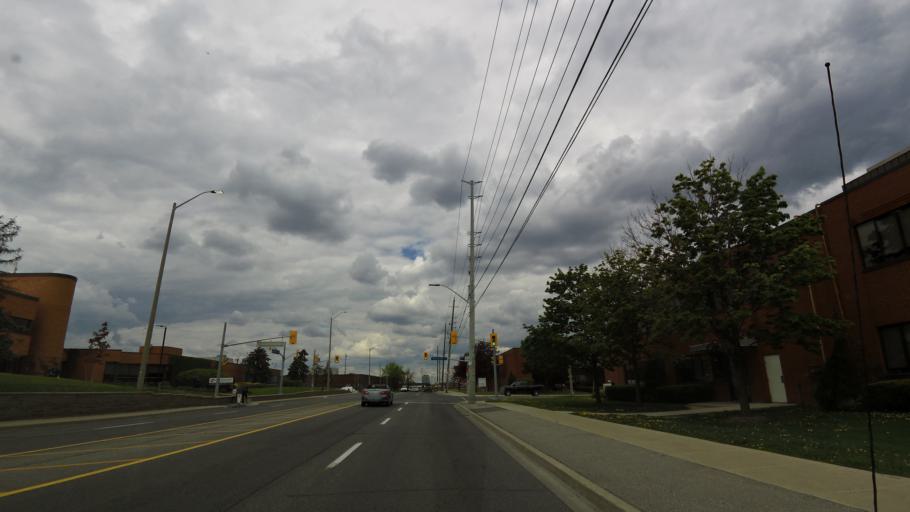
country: CA
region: Ontario
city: Mississauga
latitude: 43.5686
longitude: -79.6542
